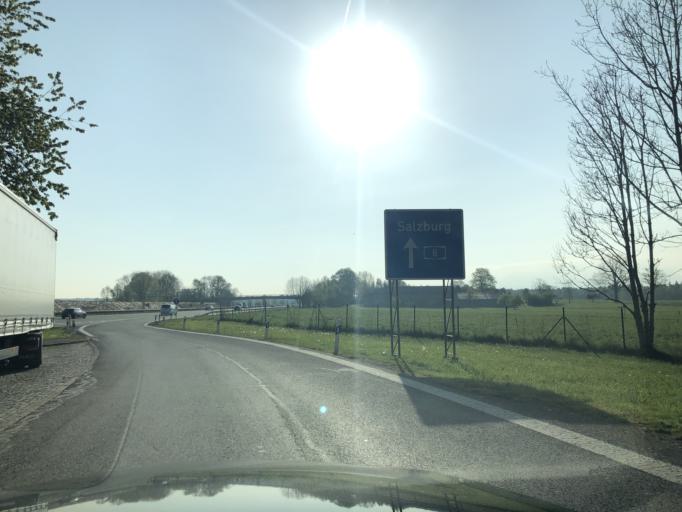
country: DE
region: Bavaria
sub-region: Upper Bavaria
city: Bad Aibling
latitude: 47.8215
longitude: 11.9807
